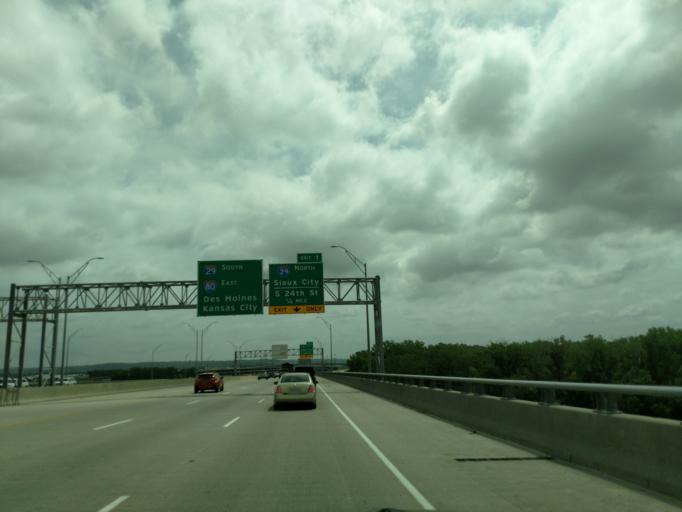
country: US
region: Nebraska
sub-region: Douglas County
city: Omaha
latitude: 41.2315
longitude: -95.9121
